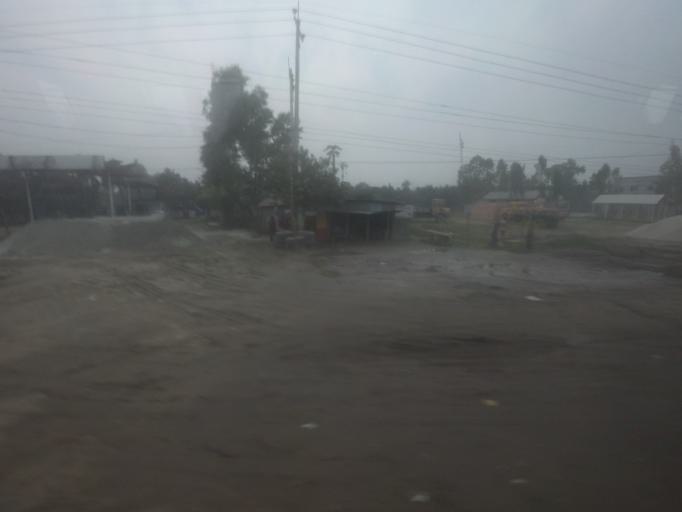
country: BD
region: Dhaka
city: Tangail
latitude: 24.3125
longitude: 89.9225
